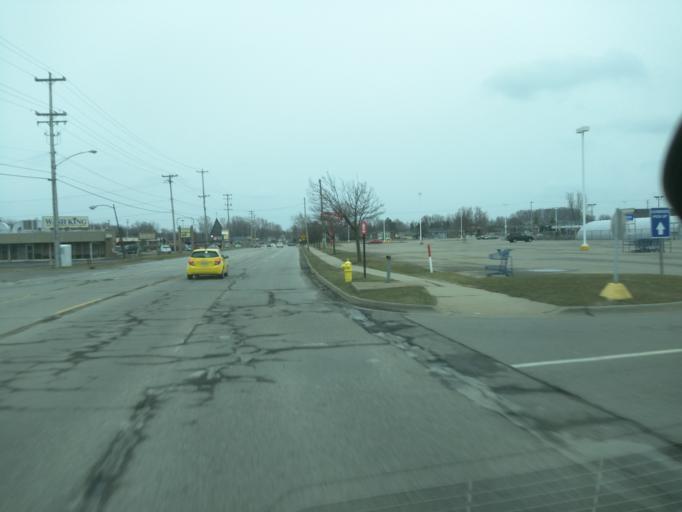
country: US
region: Michigan
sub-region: Eaton County
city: Waverly
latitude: 42.7398
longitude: -84.6219
